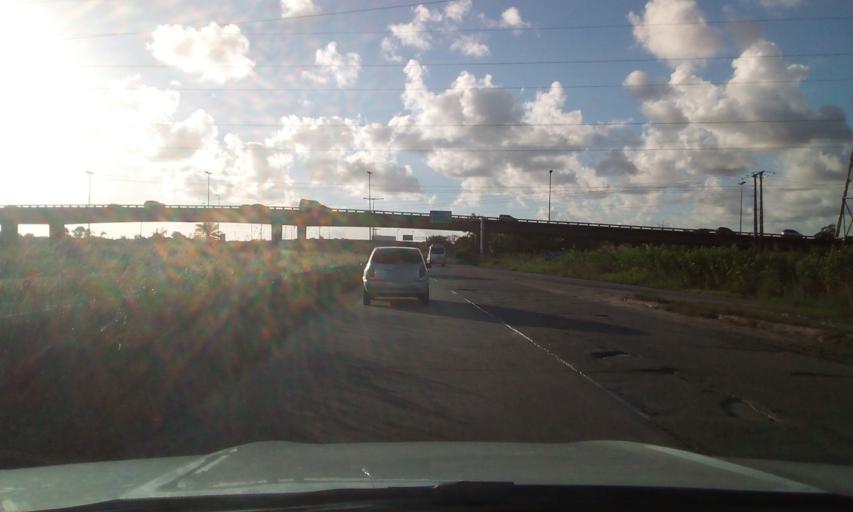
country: BR
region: Pernambuco
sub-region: Recife
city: Recife
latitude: -8.0681
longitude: -34.9412
